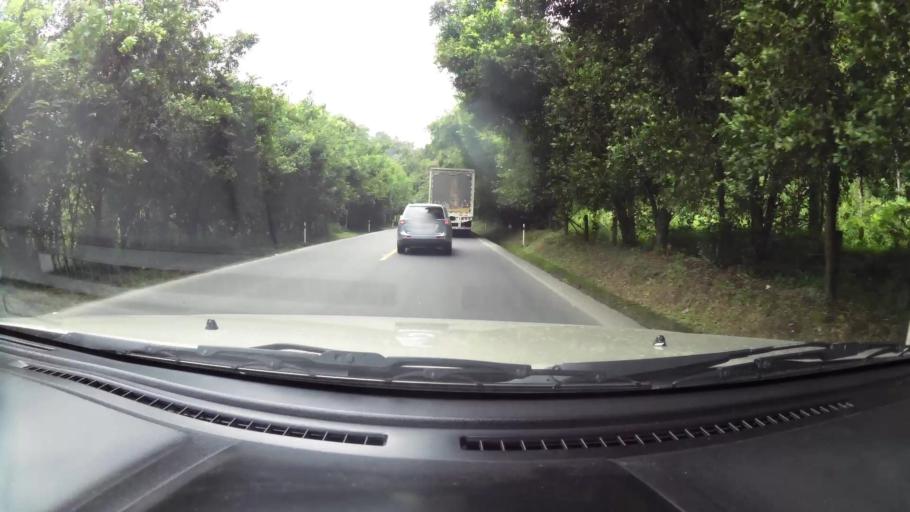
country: EC
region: Santo Domingo de los Tsachilas
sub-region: Canton Santo Domingo de los Colorados
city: Santo Domingo de los Colorados
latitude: -0.2966
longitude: -79.0573
